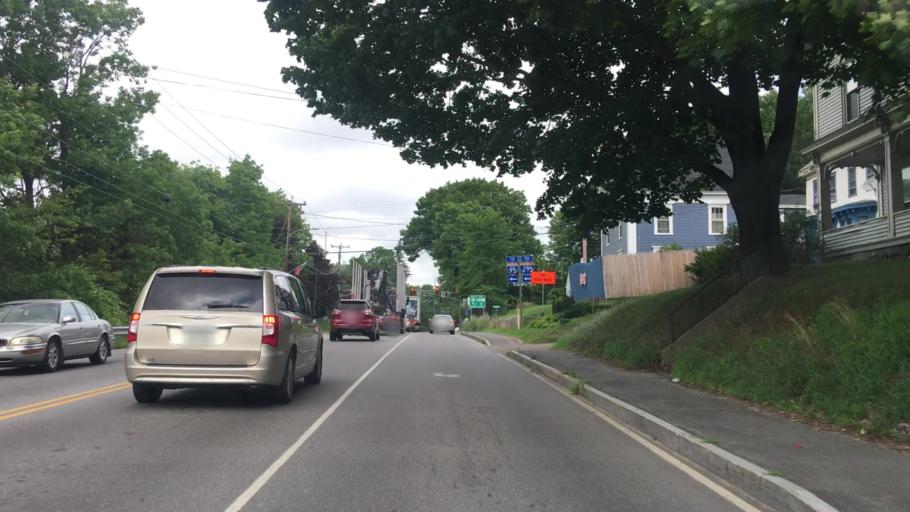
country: US
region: Maine
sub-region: Kennebec County
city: Randolph
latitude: 44.2319
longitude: -69.7674
